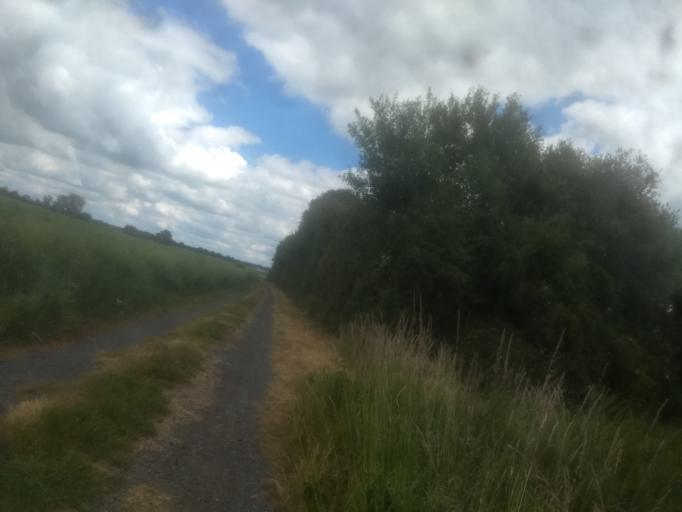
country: FR
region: Nord-Pas-de-Calais
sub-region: Departement du Pas-de-Calais
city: Beaurains
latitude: 50.2136
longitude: 2.7978
